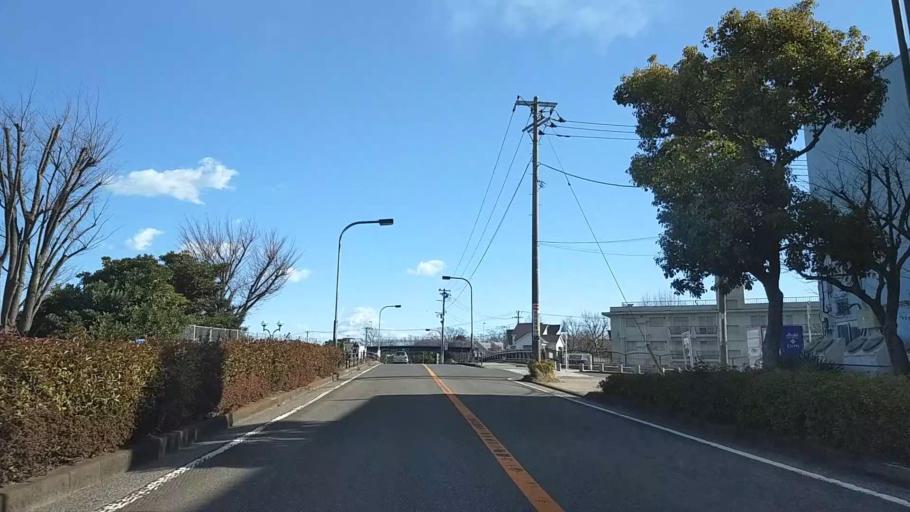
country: JP
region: Kanagawa
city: Yokosuka
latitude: 35.3265
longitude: 139.6284
